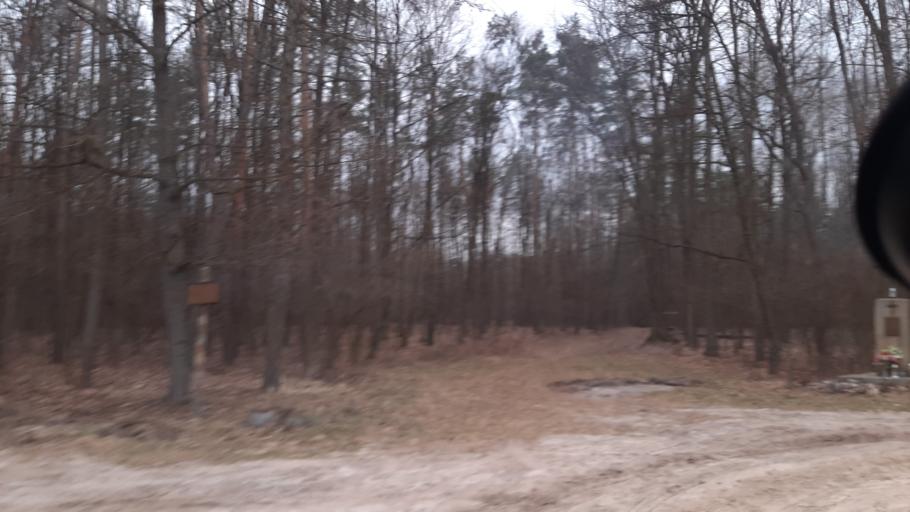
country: PL
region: Lublin Voivodeship
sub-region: Powiat lubelski
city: Garbow
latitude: 51.4006
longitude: 22.3880
